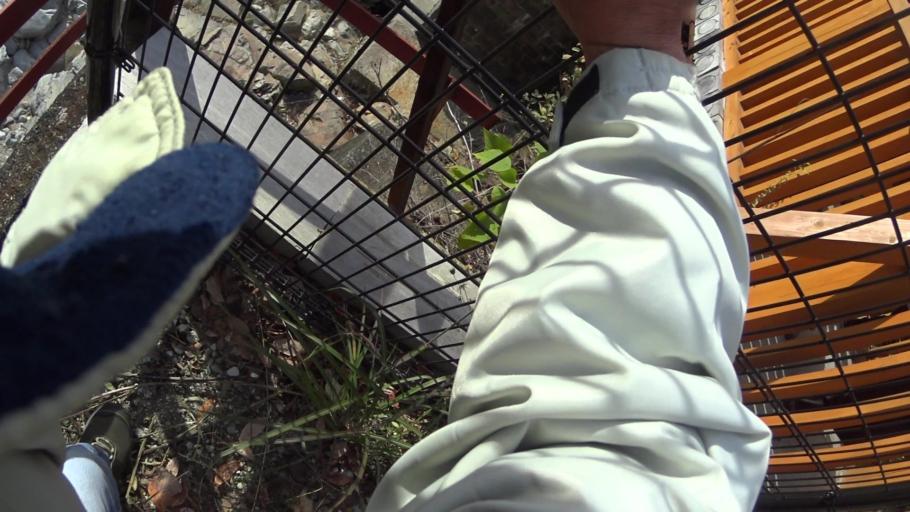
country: JP
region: Hyogo
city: Takarazuka
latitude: 34.8270
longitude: 135.3230
